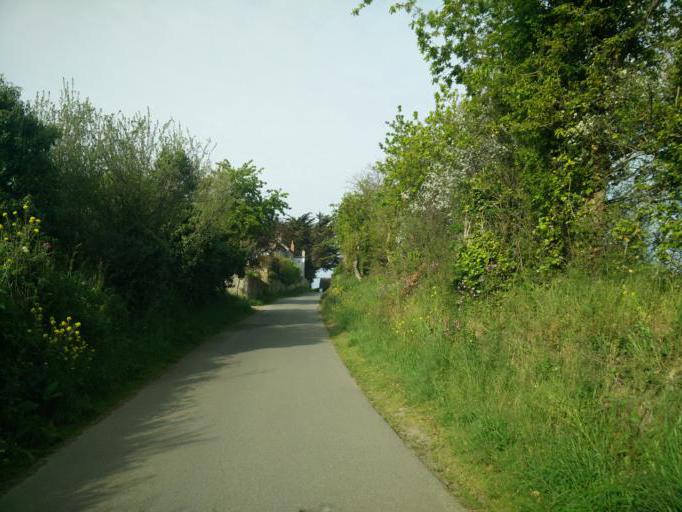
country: FR
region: Brittany
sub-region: Departement des Cotes-d'Armor
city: Lezardrieux
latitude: 48.8287
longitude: -3.0860
